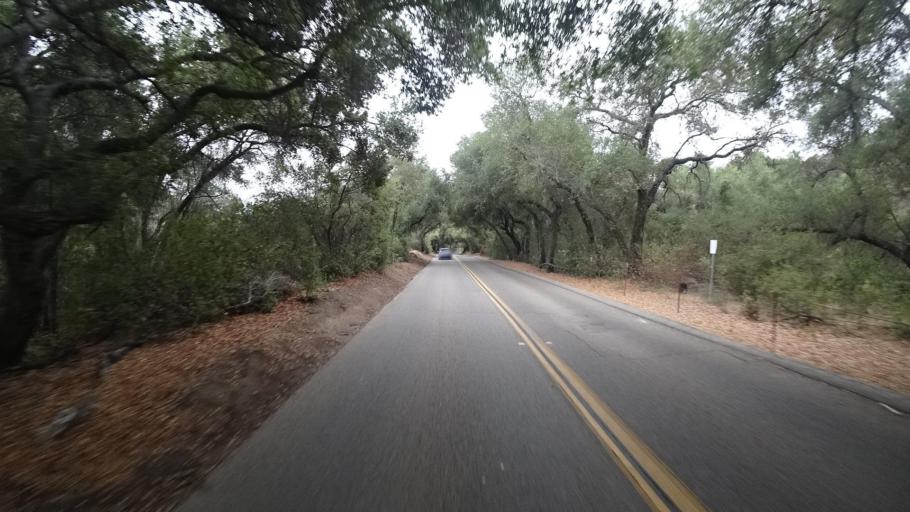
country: US
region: California
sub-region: San Diego County
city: Escondido
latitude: 33.0815
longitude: -117.1148
